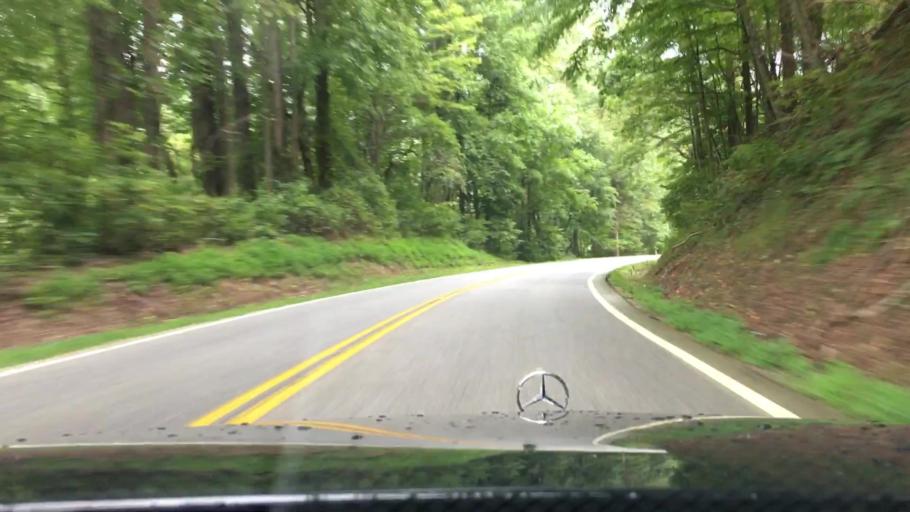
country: US
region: Virginia
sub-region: Nelson County
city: Nellysford
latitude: 37.8484
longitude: -78.9268
